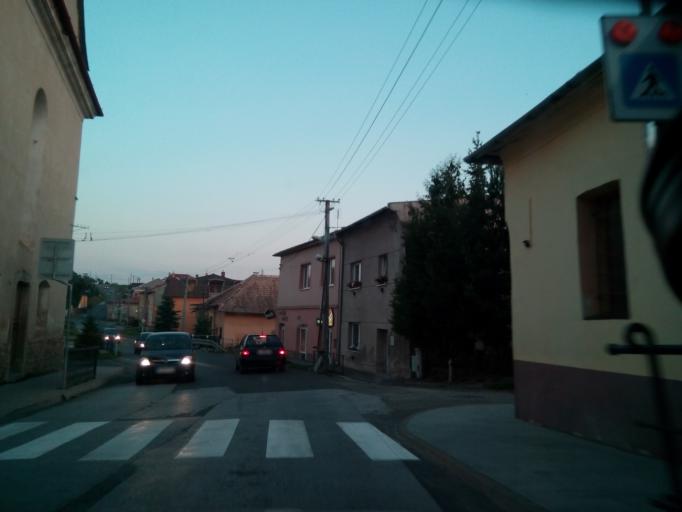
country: SK
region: Presovsky
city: Lubica
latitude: 49.0872
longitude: 20.4253
